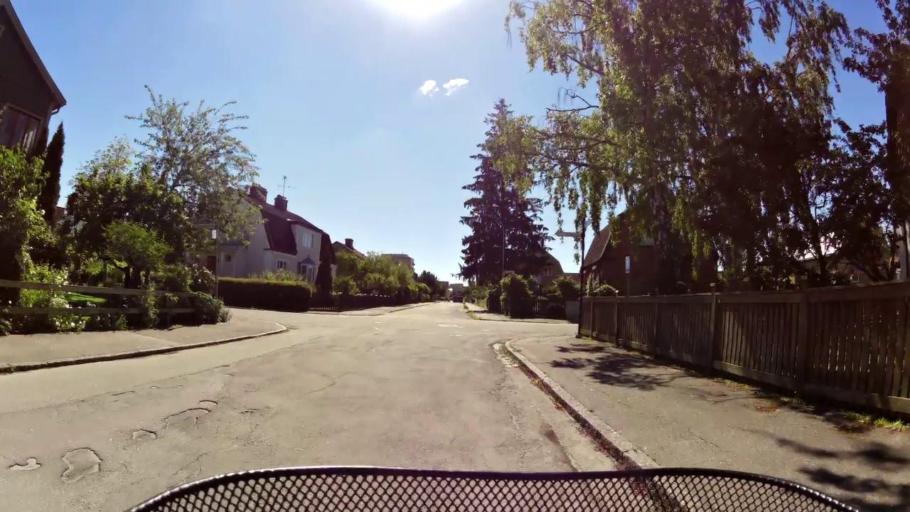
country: SE
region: OEstergoetland
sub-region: Linkopings Kommun
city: Linkoping
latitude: 58.4064
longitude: 15.6391
